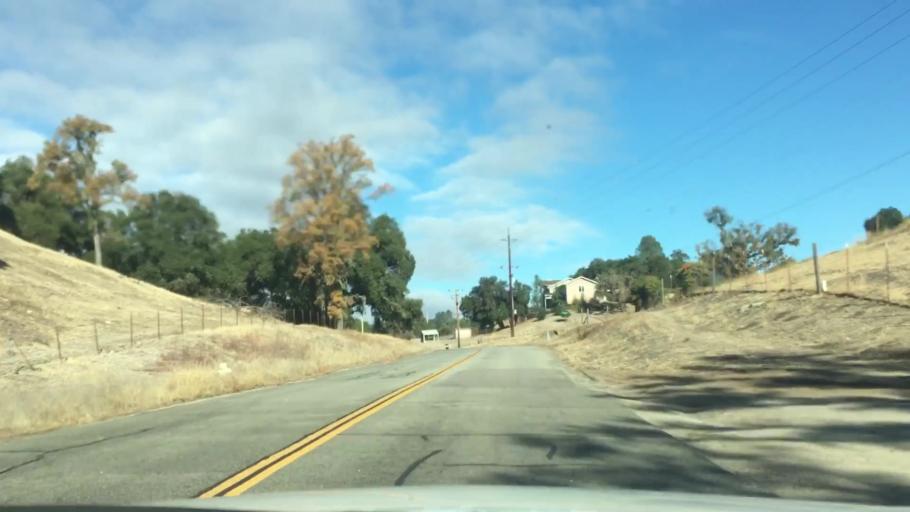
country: US
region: California
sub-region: San Luis Obispo County
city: Atascadero
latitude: 35.4434
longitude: -120.6455
